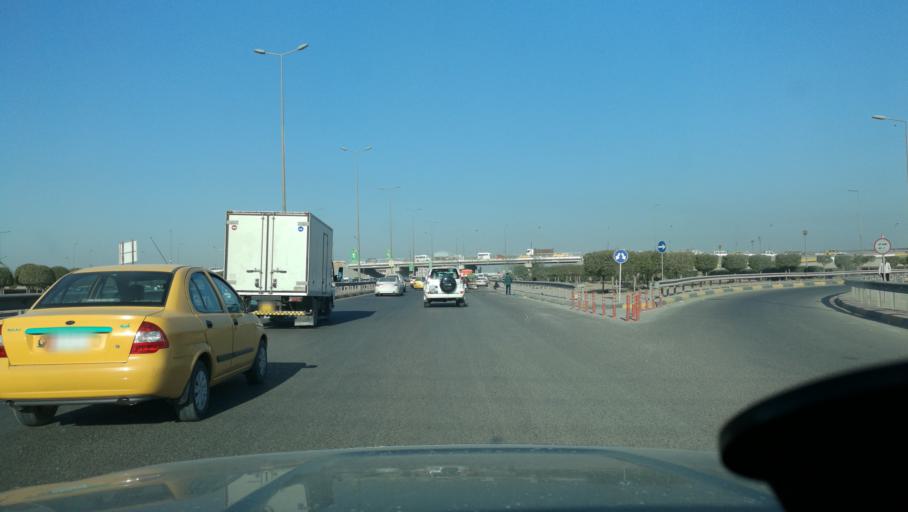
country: IQ
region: Basra Governorate
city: Al Basrah al Qadimah
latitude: 30.4843
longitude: 47.8033
